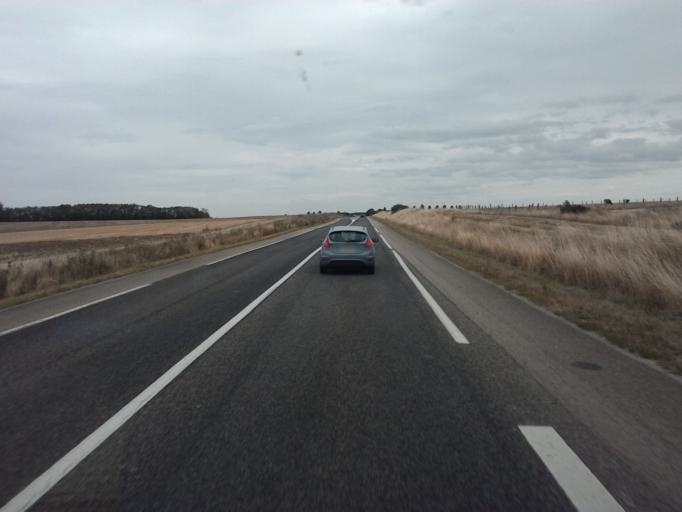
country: FR
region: Lorraine
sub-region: Departement de Meurthe-et-Moselle
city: Bainville-sur-Madon
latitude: 48.5772
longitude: 6.0805
